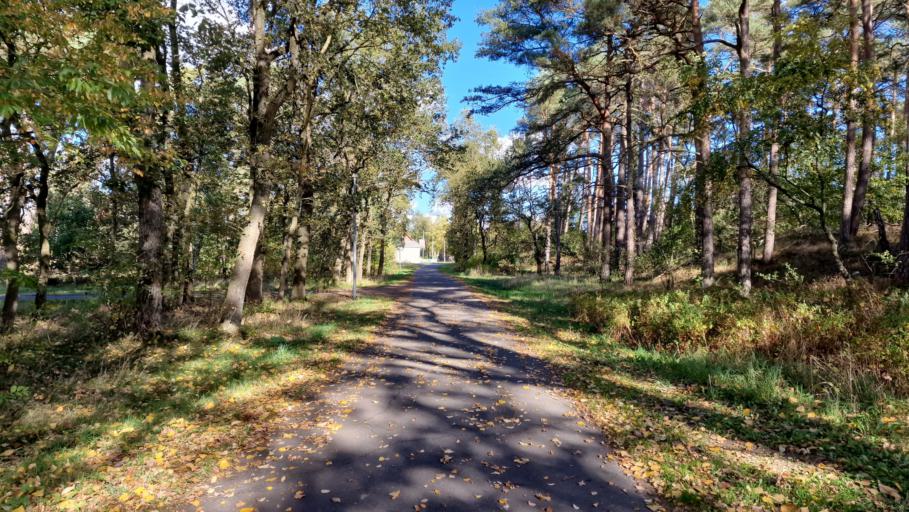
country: DE
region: Mecklenburg-Vorpommern
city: Eldena
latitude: 53.1644
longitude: 11.4479
